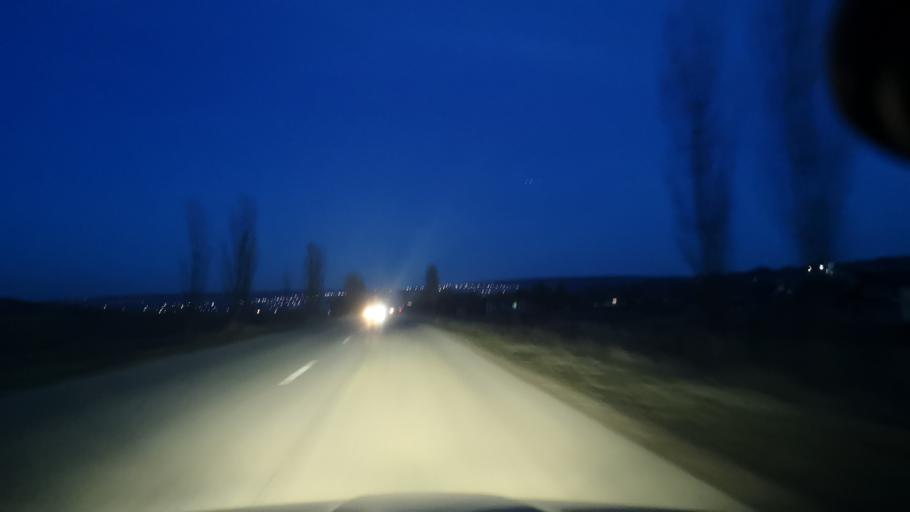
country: MD
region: Orhei
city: Orhei
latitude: 47.3434
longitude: 28.7578
